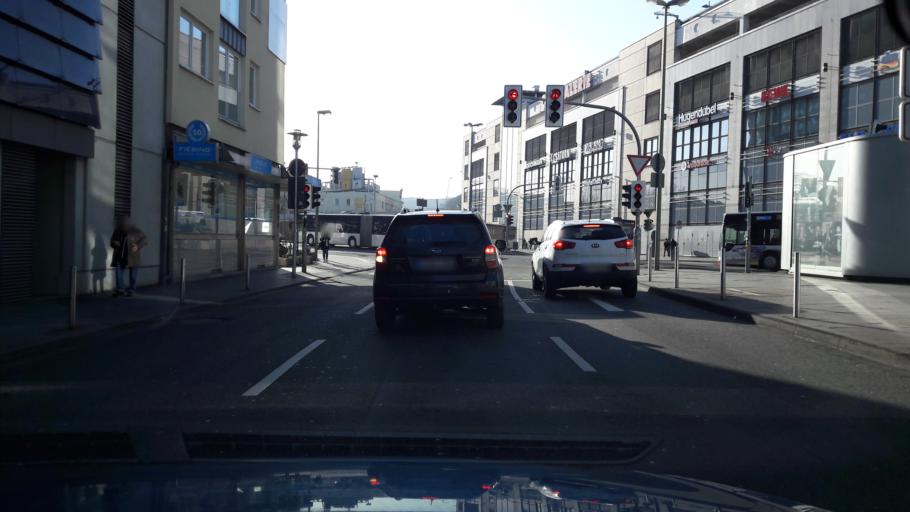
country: DE
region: North Rhine-Westphalia
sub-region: Regierungsbezirk Arnsberg
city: Siegen
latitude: 50.8738
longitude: 8.0161
